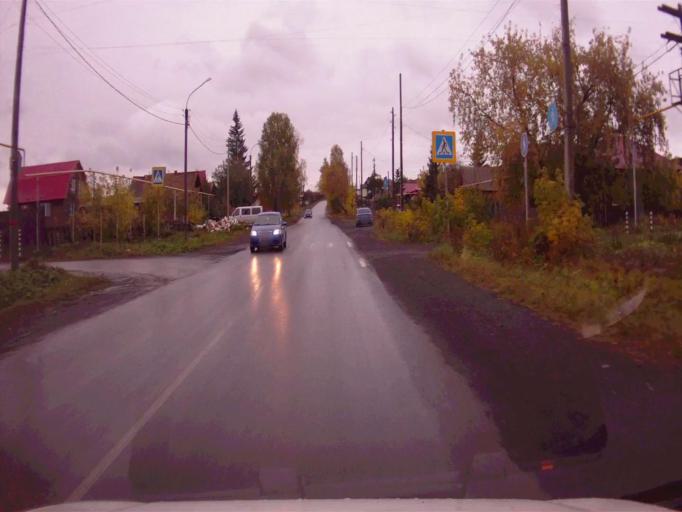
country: RU
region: Chelyabinsk
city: Verkhniy Ufaley
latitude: 56.0493
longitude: 60.2068
